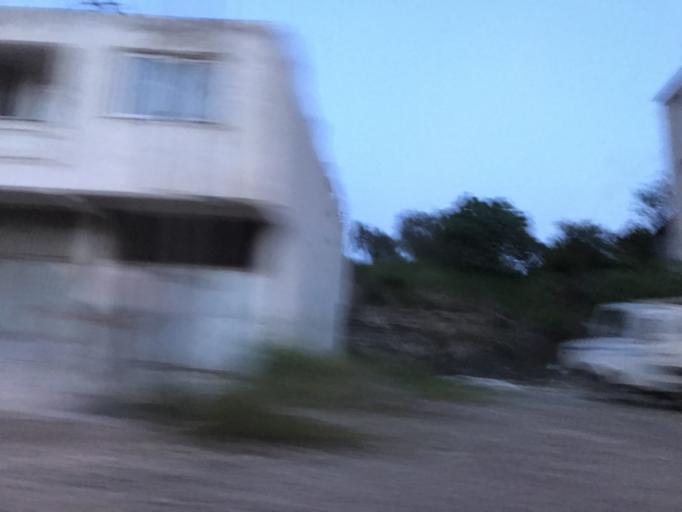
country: TR
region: Hatay
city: Karacay
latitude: 36.1570
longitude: 36.0959
